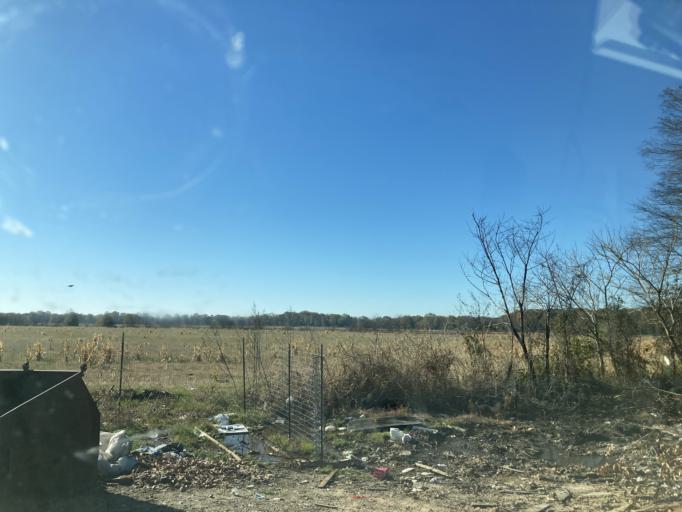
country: US
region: Mississippi
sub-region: Madison County
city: Kearney Park
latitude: 32.6040
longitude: -90.4042
